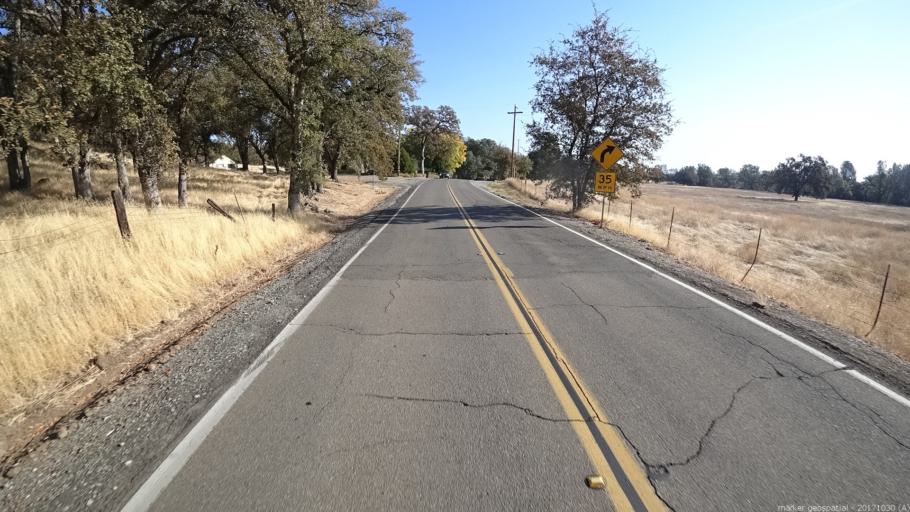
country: US
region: California
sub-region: Shasta County
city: Palo Cedro
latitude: 40.5658
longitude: -122.2127
